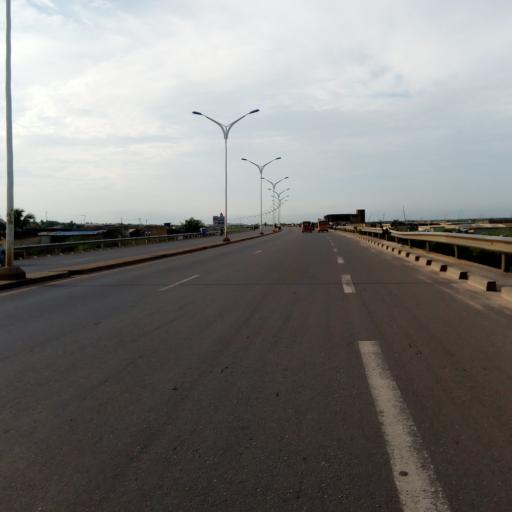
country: TG
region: Maritime
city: Lome
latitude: 6.1819
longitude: 1.2804
